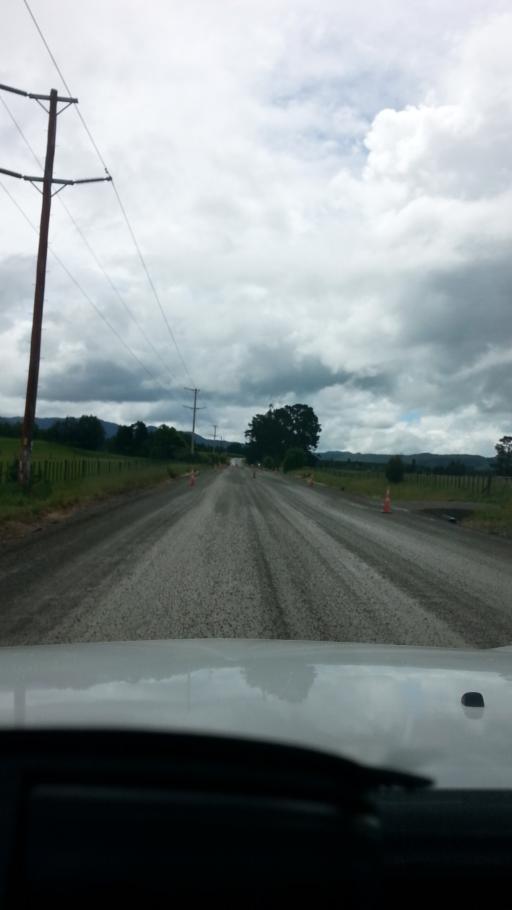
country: NZ
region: Wellington
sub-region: Masterton District
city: Masterton
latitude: -40.8300
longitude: 175.6269
